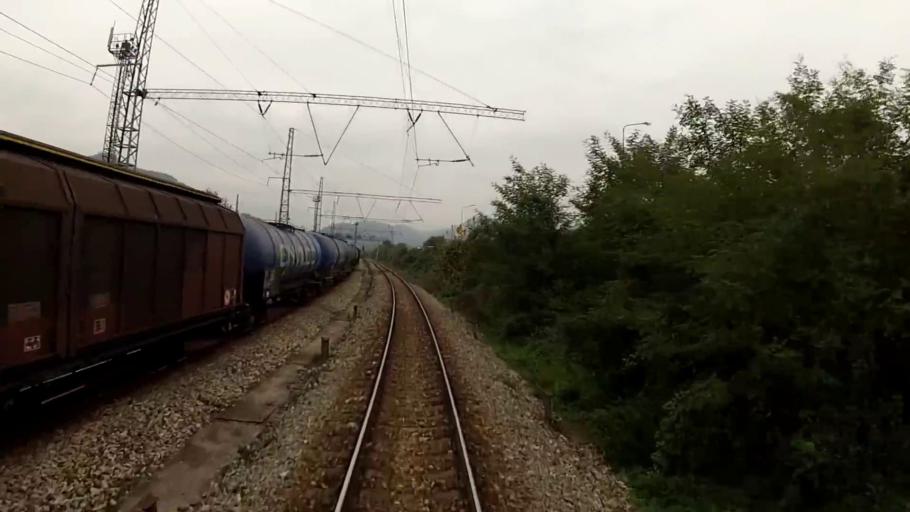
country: RS
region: Central Serbia
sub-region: Pirotski Okrug
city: Dimitrovgrad
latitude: 42.9915
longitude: 22.8507
